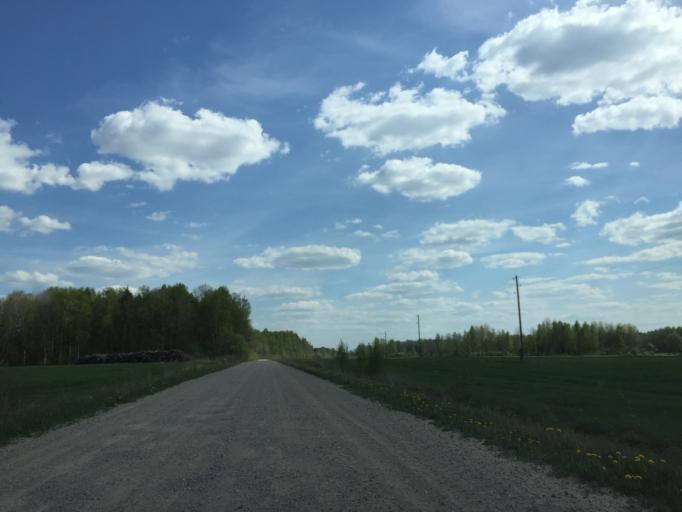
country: LV
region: Limbazu Rajons
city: Limbazi
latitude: 57.3991
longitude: 24.6283
